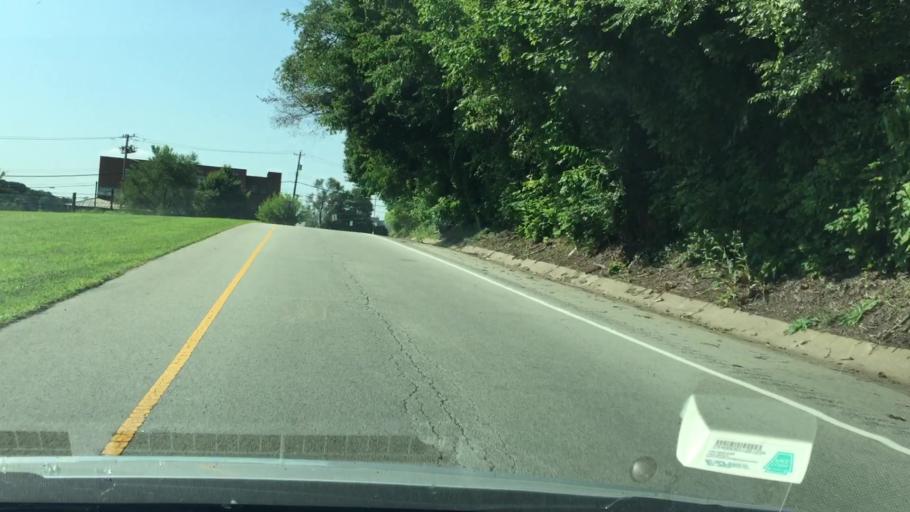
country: US
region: Pennsylvania
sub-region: Allegheny County
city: West View
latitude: 40.5548
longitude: -80.0223
